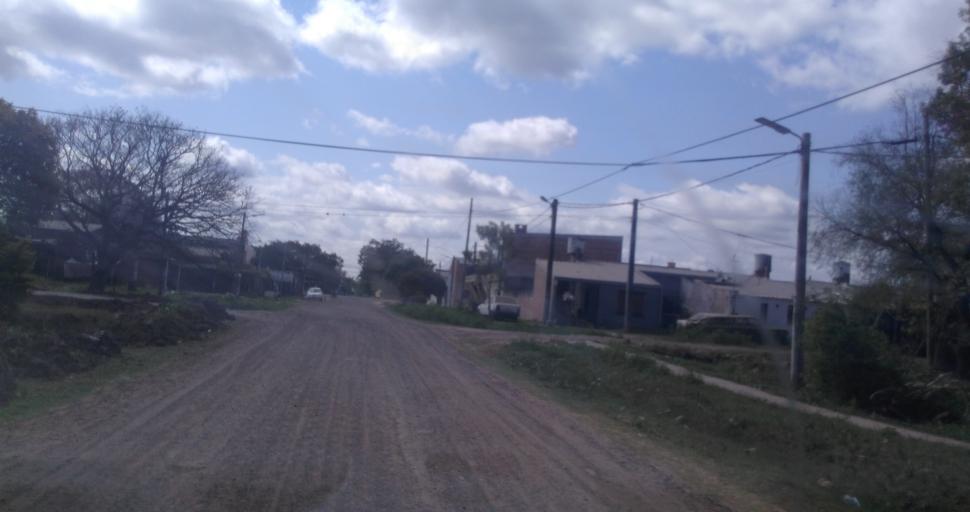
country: AR
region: Chaco
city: Fontana
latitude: -27.4265
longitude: -59.0308
